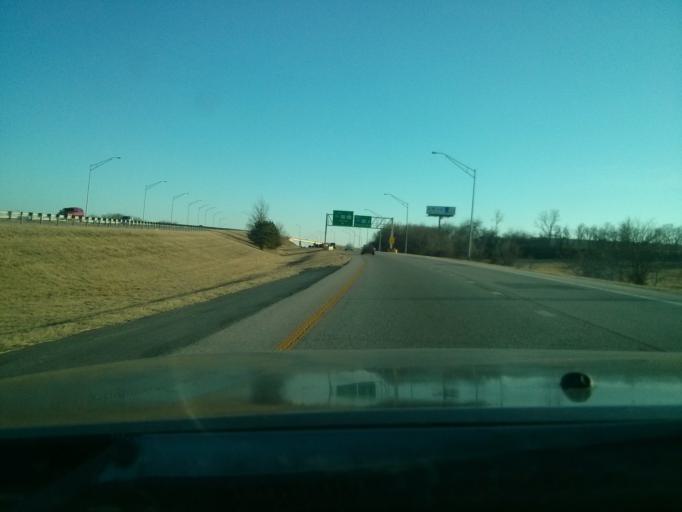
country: US
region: Oklahoma
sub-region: Tulsa County
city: Owasso
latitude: 36.1686
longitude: -95.8847
